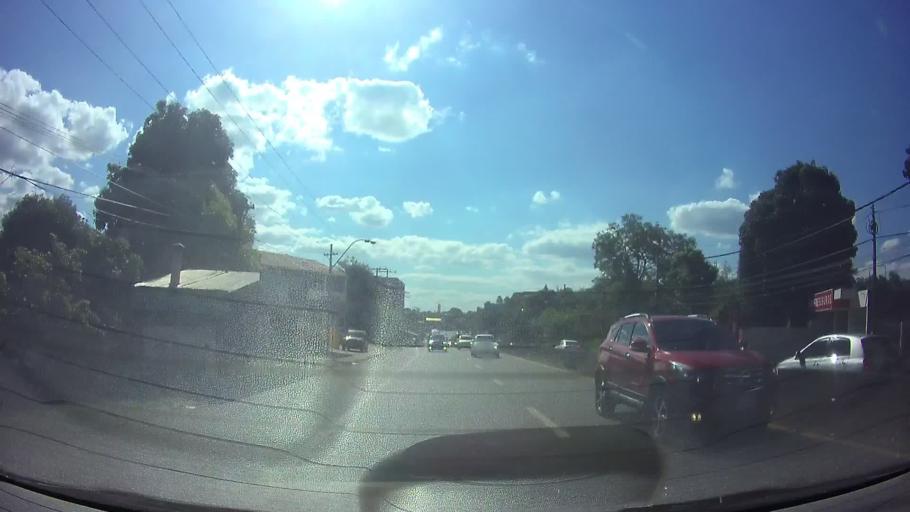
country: PY
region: Central
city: Itaugua
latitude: -25.3965
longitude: -57.3439
